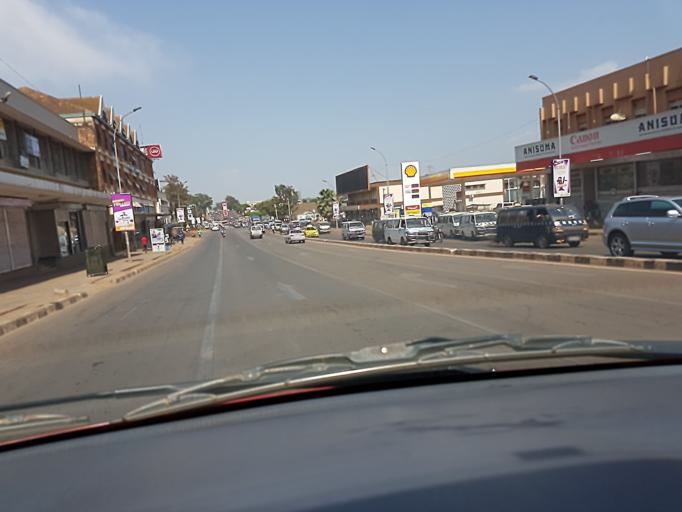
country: UG
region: Central Region
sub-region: Kampala District
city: Kampala
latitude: 0.3159
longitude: 32.5922
